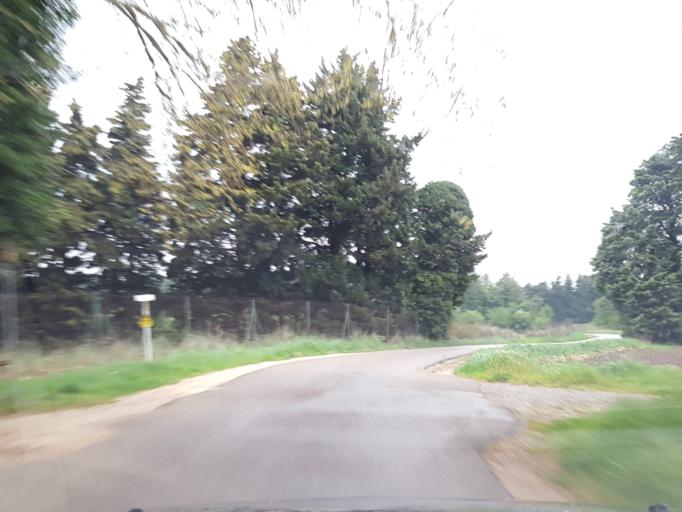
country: FR
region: Provence-Alpes-Cote d'Azur
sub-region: Departement du Vaucluse
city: Saint-Saturnin-les-Avignon
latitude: 43.9751
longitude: 4.9296
